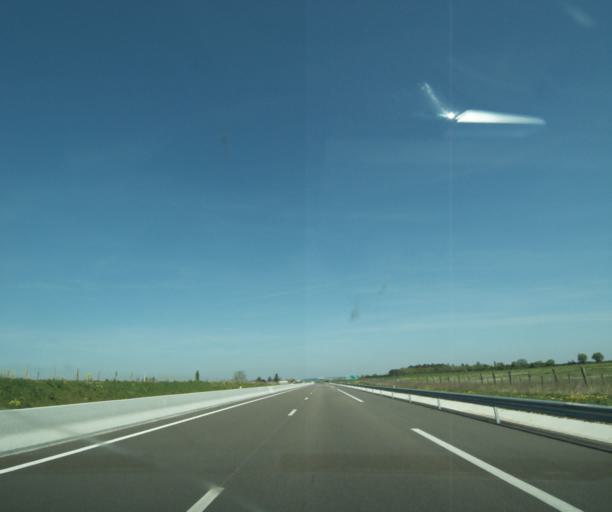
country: FR
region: Bourgogne
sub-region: Departement de la Nievre
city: Saint-Pierre-le-Moutier
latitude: 46.8091
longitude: 3.1218
